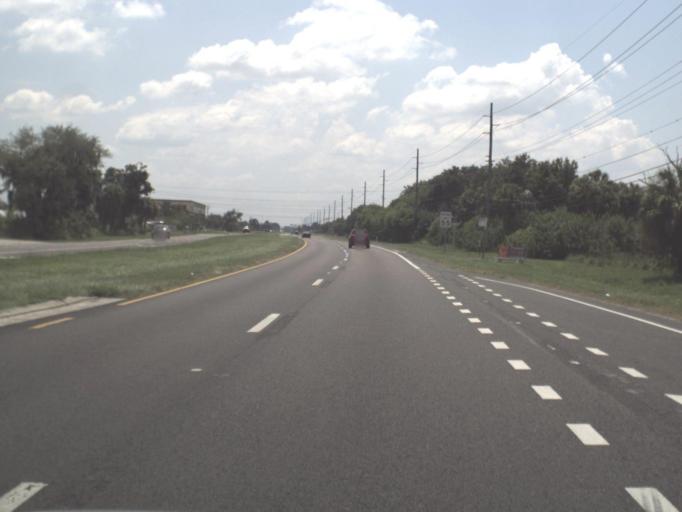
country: US
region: Florida
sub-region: Hillsborough County
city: Gibsonton
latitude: 27.8144
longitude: -82.3842
